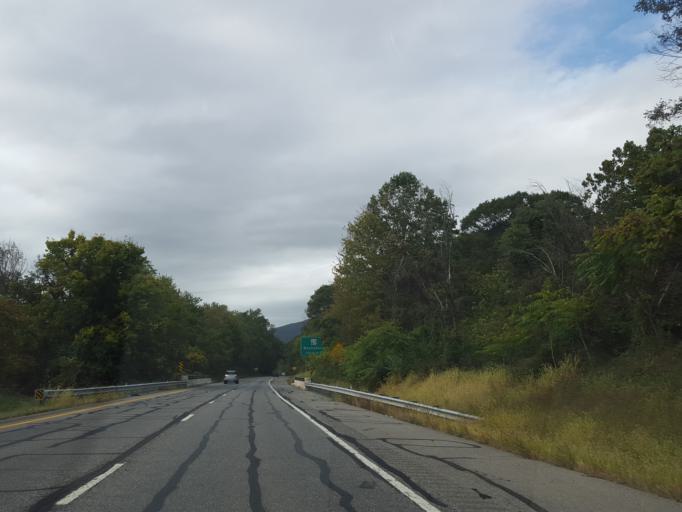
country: US
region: Maryland
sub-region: Frederick County
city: Brunswick
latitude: 39.3310
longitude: -77.6656
